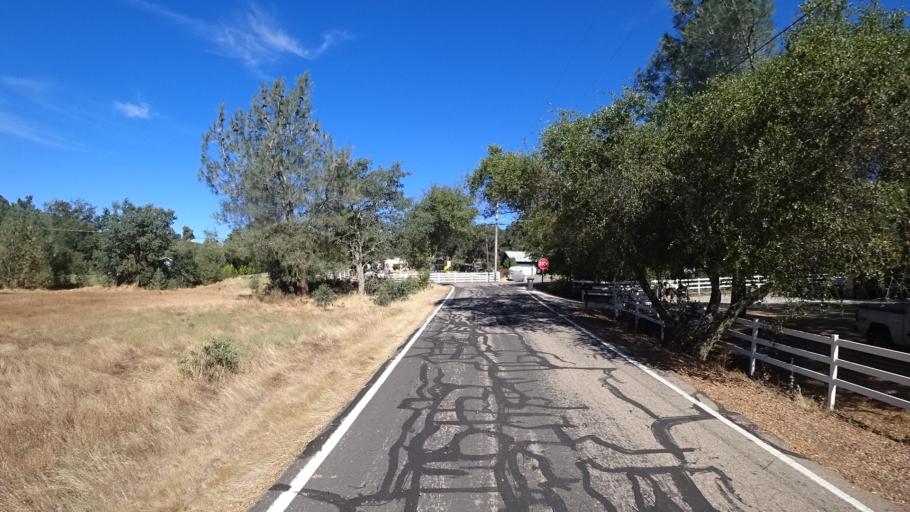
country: US
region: California
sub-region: Calaveras County
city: Valley Springs
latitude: 38.1655
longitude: -120.8560
